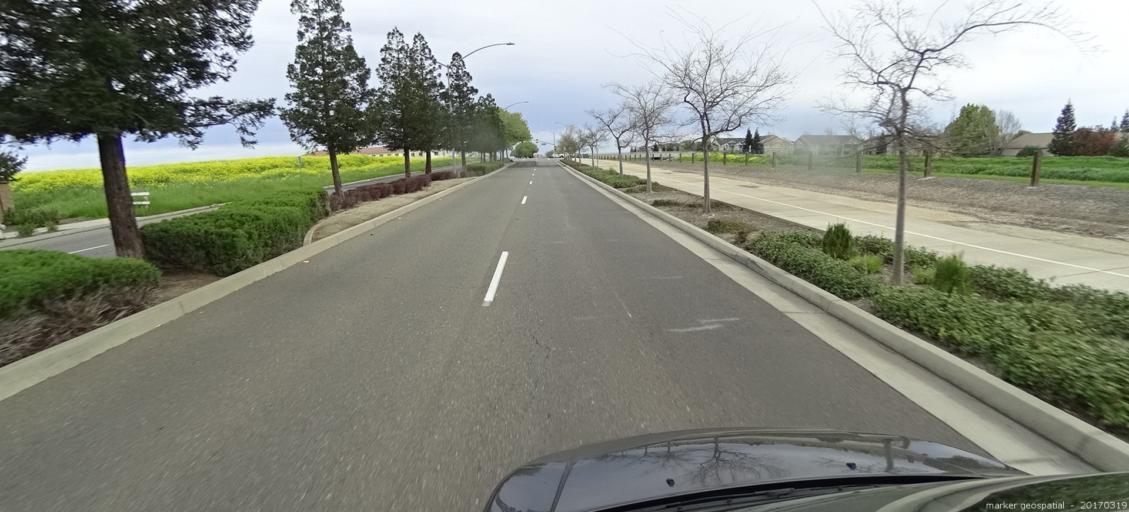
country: US
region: California
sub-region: Sacramento County
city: Elverta
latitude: 38.6800
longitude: -121.5078
